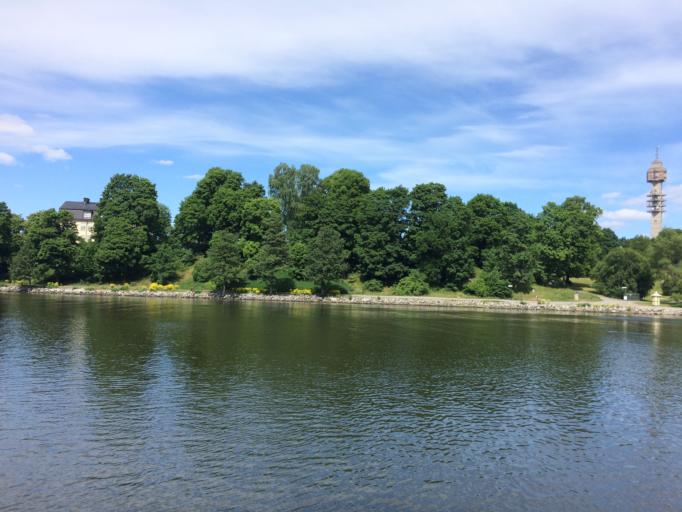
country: SE
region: Stockholm
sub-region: Stockholms Kommun
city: OEstermalm
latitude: 59.3301
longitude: 18.1178
